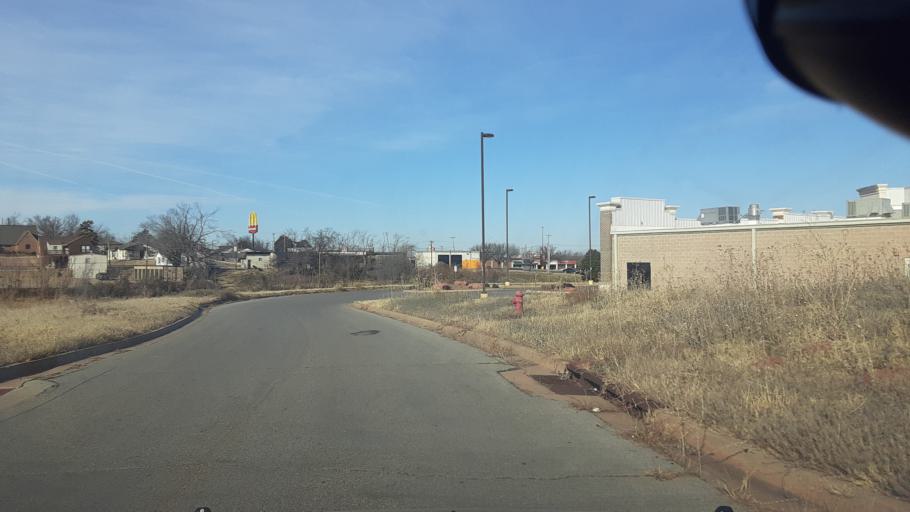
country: US
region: Oklahoma
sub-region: Logan County
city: Guthrie
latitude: 35.8601
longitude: -97.4233
